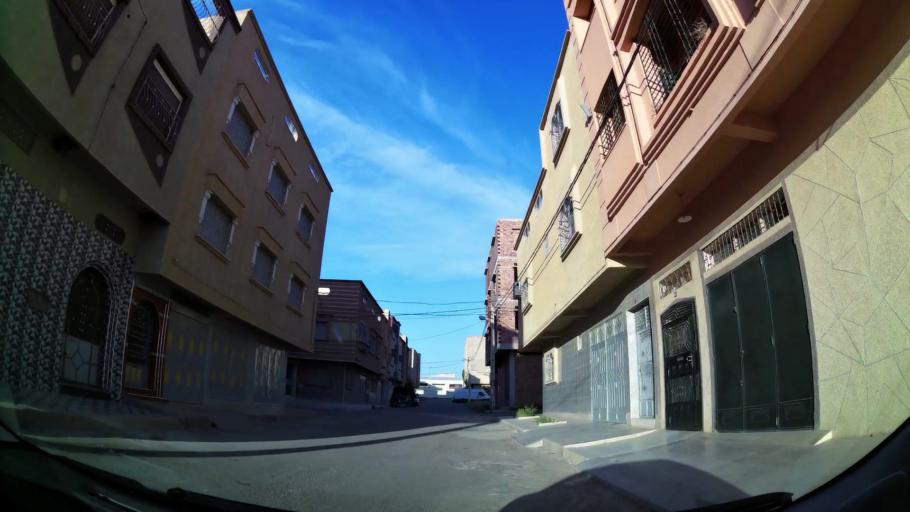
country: MA
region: Oriental
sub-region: Oujda-Angad
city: Oujda
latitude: 34.7017
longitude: -1.9178
